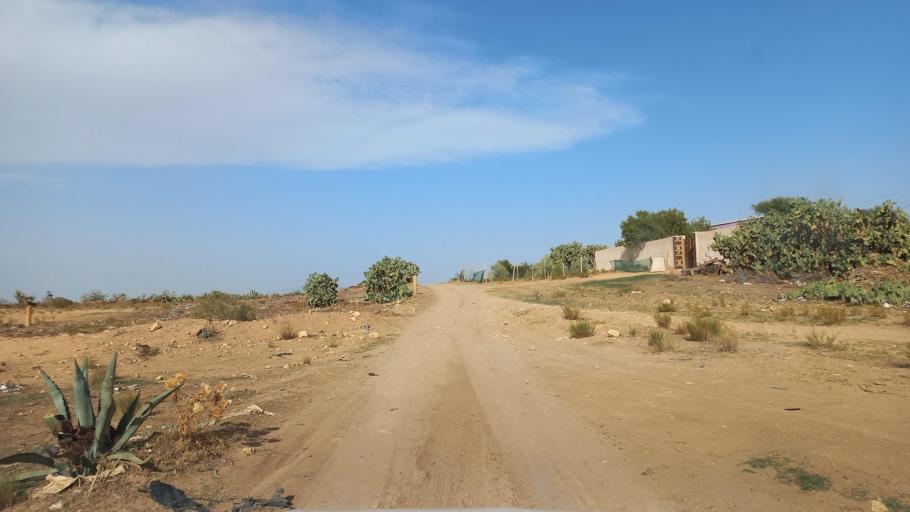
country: TN
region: Al Qasrayn
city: Kasserine
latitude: 35.2106
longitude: 8.9698
